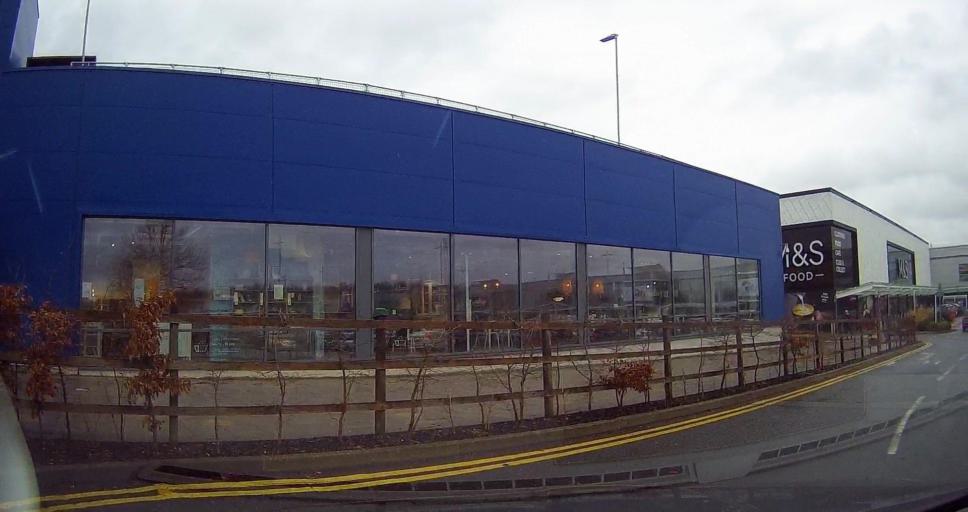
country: GB
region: England
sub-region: Nottinghamshire
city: Awsworth
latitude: 53.0030
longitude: -1.2831
